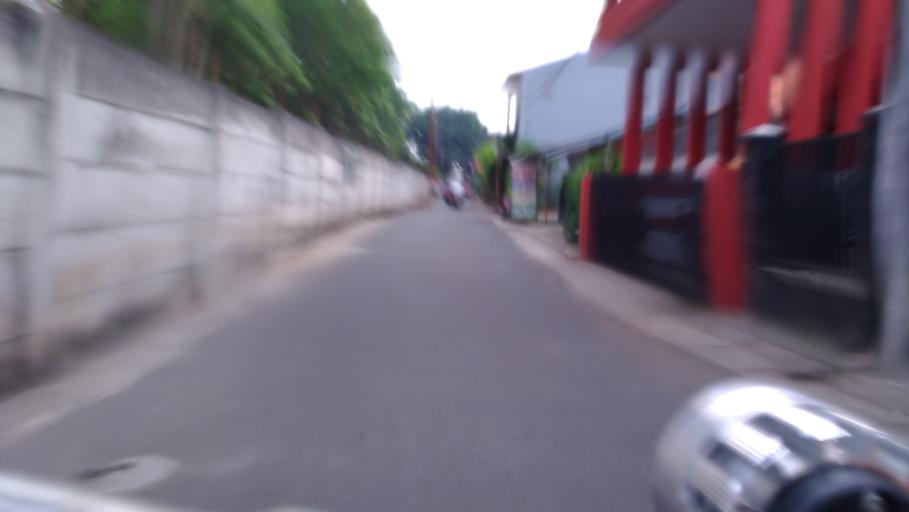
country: ID
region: West Java
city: Depok
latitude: -6.3523
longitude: 106.8677
